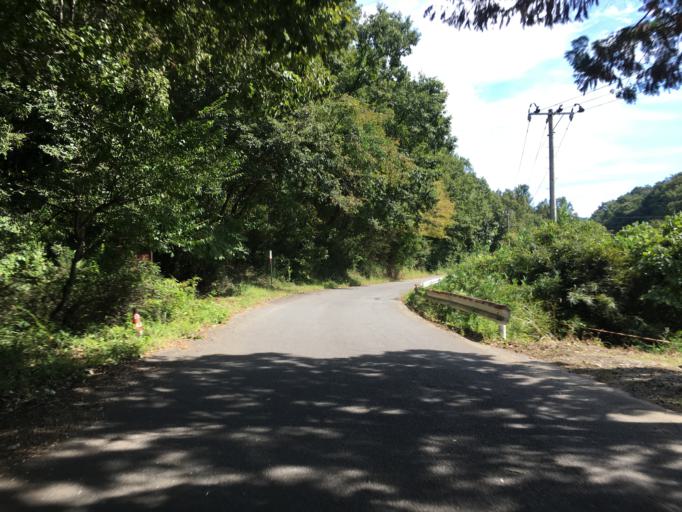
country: JP
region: Fukushima
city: Fukushima-shi
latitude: 37.7001
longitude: 140.5136
